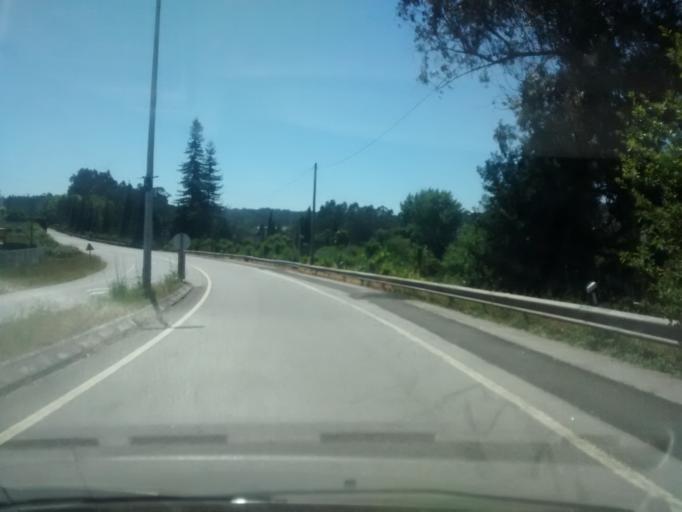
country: PT
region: Braga
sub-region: Barcelos
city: Vila Frescainha
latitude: 41.5216
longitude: -8.6334
